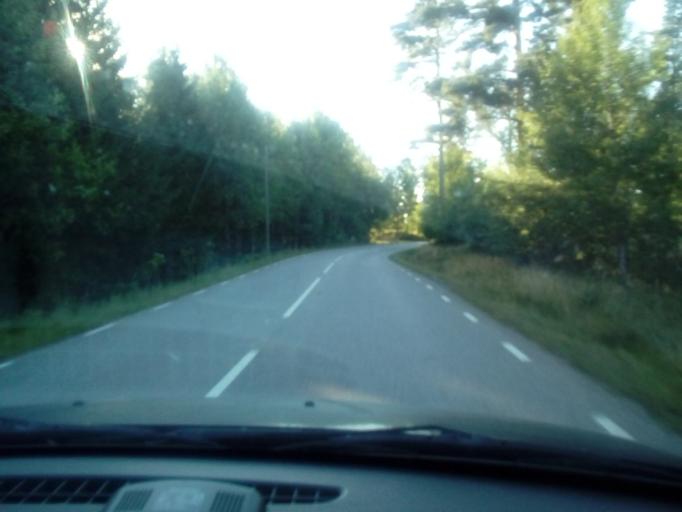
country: SE
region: Kalmar
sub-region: Vasterviks Kommun
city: Gamleby
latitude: 57.7905
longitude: 16.3825
